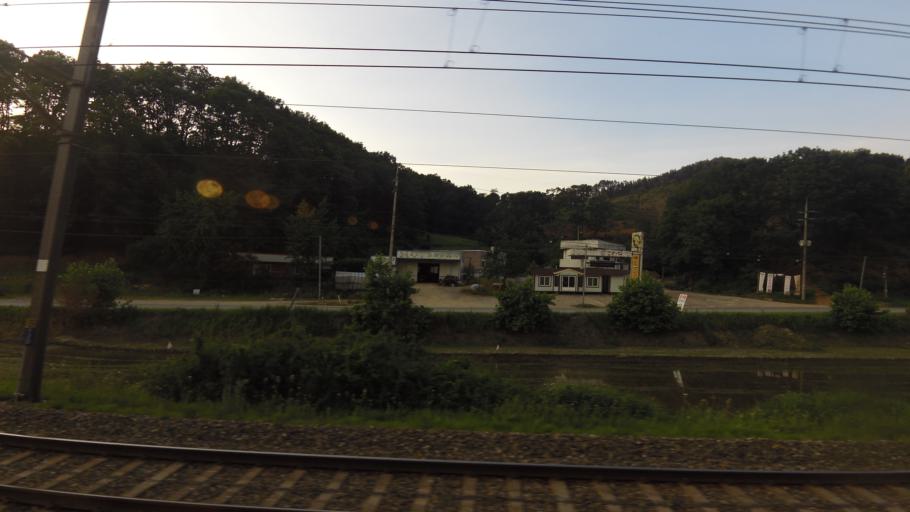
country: KR
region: Chungcheongnam-do
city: Cheonan
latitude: 36.6654
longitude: 127.2476
